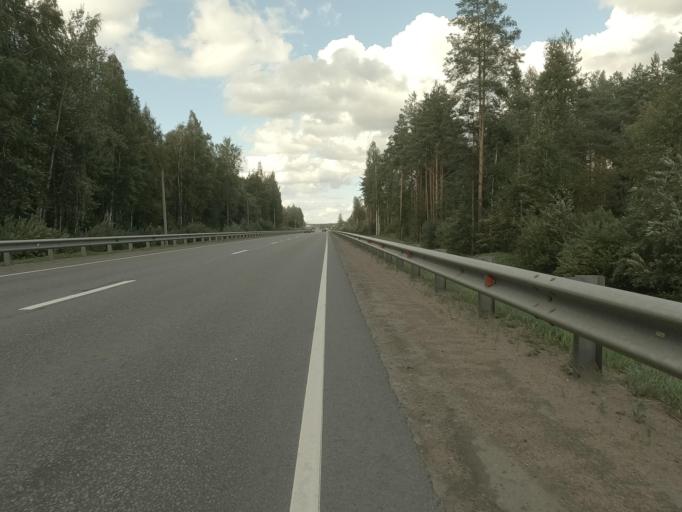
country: RU
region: Leningrad
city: Mga
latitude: 59.7410
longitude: 31.0781
